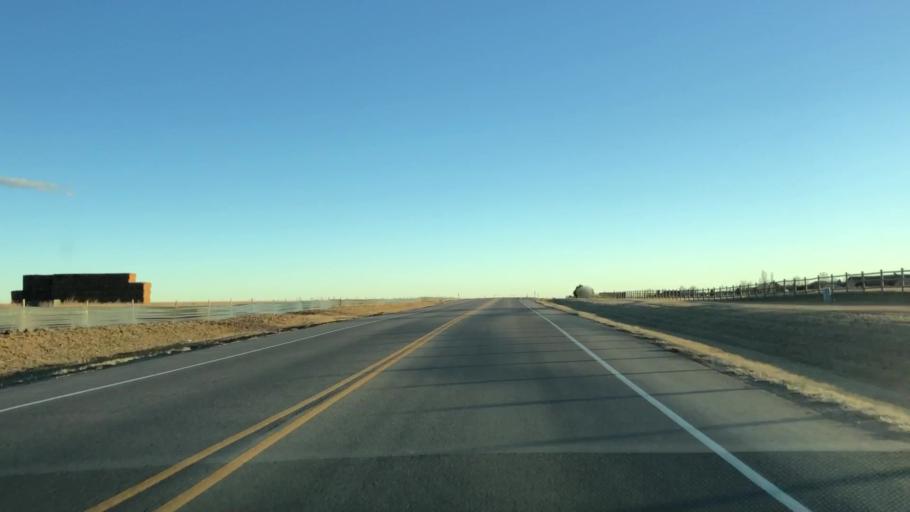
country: US
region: Colorado
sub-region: Weld County
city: Windsor
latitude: 40.4433
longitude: -104.9442
